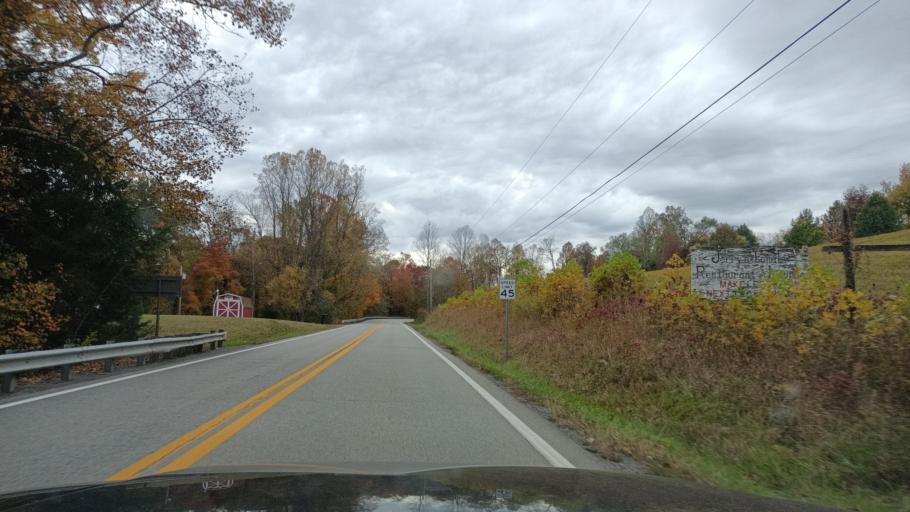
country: US
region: West Virginia
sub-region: Taylor County
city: Grafton
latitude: 39.3422
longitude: -79.9946
